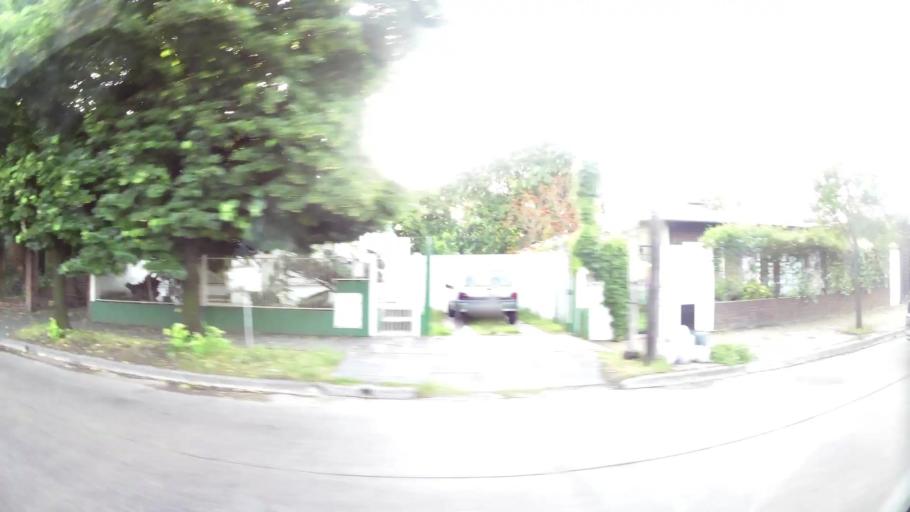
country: AR
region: Buenos Aires
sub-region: Partido de Moron
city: Moron
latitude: -34.6589
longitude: -58.6300
